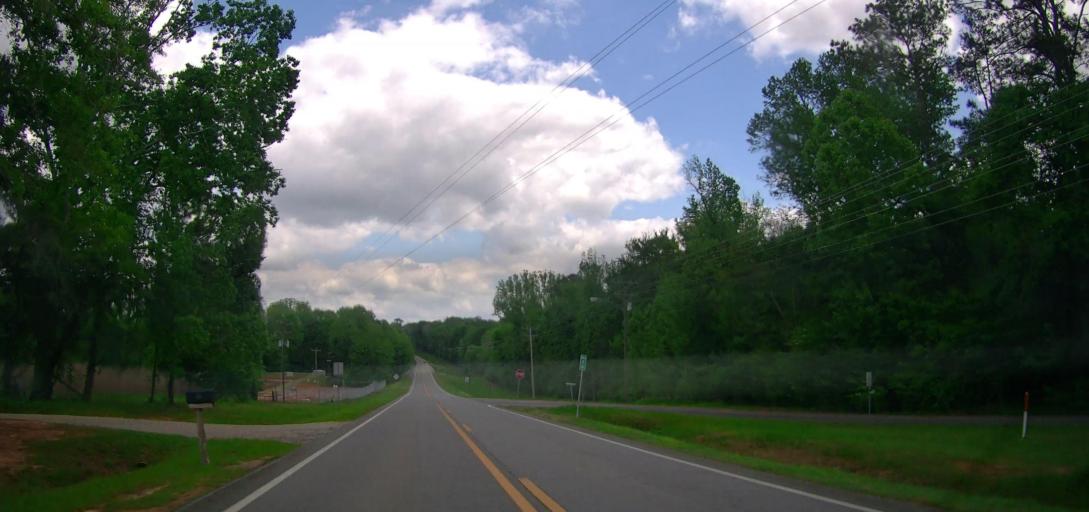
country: US
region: Georgia
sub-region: Laurens County
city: Dublin
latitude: 32.5502
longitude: -83.0577
